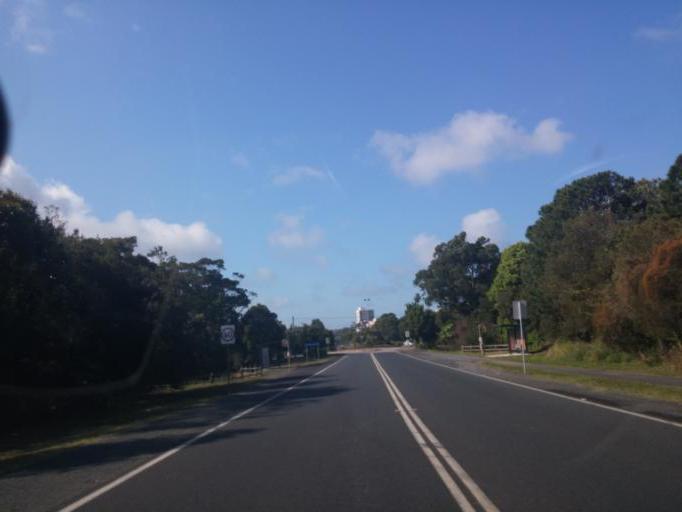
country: AU
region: New South Wales
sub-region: Coffs Harbour
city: Coffs Harbour
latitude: -30.2901
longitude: 153.1346
